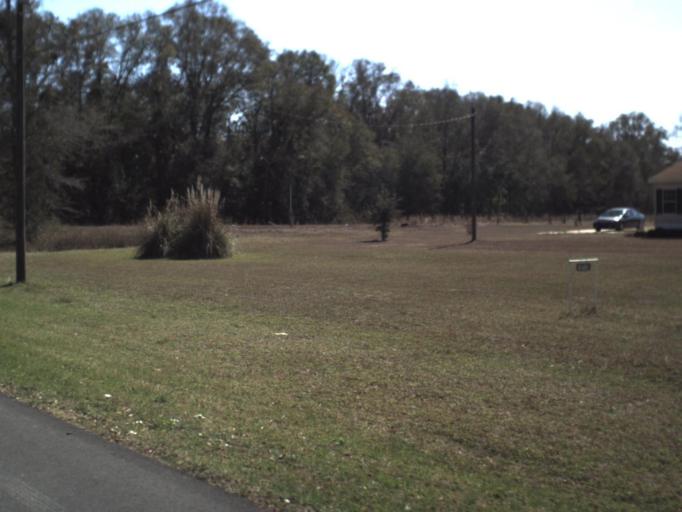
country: US
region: Florida
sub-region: Jackson County
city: Malone
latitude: 30.8646
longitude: -85.1163
